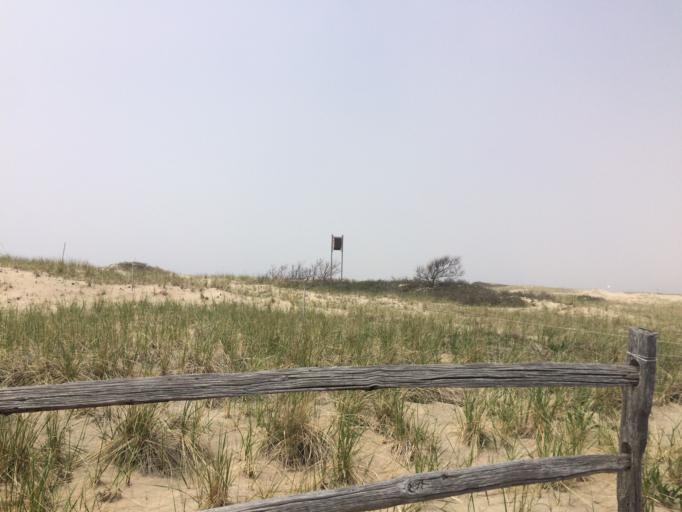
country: US
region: Massachusetts
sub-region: Barnstable County
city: Provincetown
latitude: 42.0625
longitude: -70.2432
